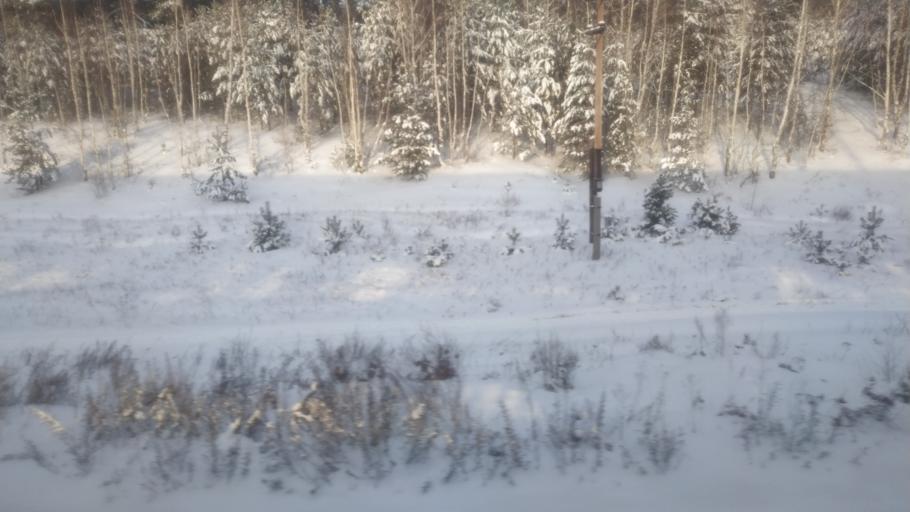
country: RU
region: Kirov
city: Krasnaya Polyana
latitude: 56.2461
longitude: 51.1678
